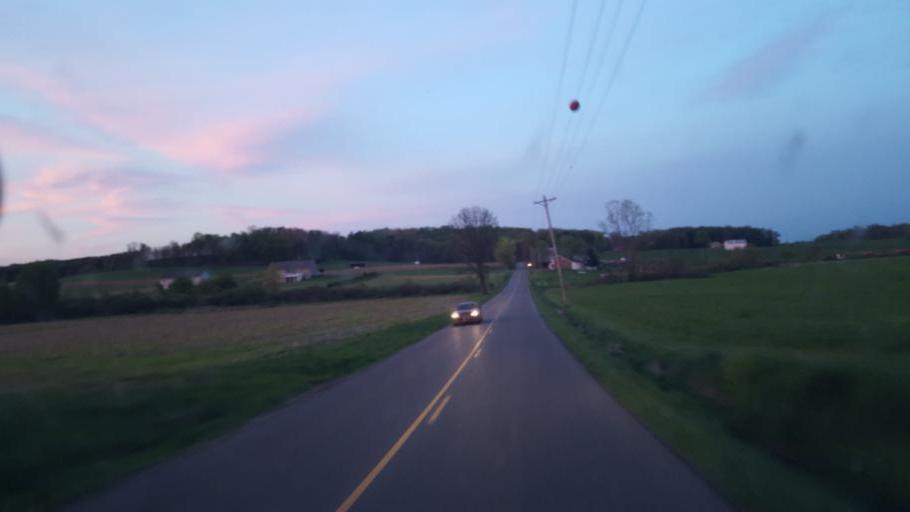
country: US
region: Ohio
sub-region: Knox County
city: Fredericktown
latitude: 40.4765
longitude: -82.4833
